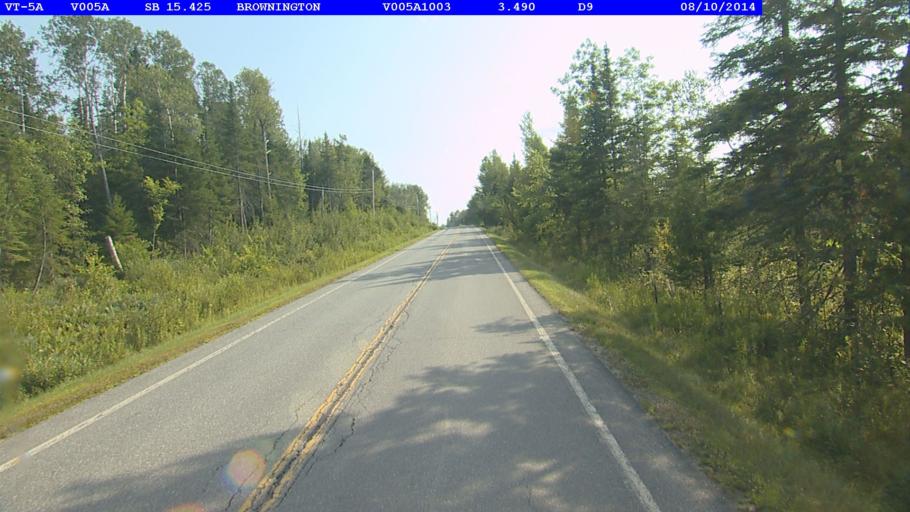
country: US
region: Vermont
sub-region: Orleans County
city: Newport
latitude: 44.8318
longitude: -72.0672
